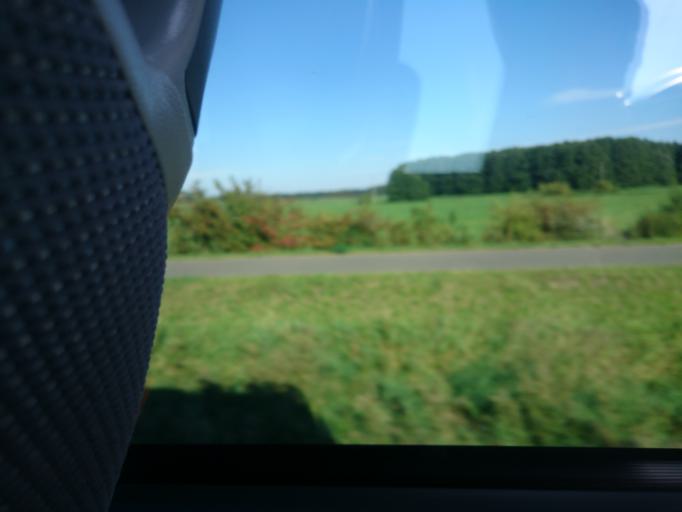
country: DE
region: Mecklenburg-Vorpommern
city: Ducherow
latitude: 53.7435
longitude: 13.7835
